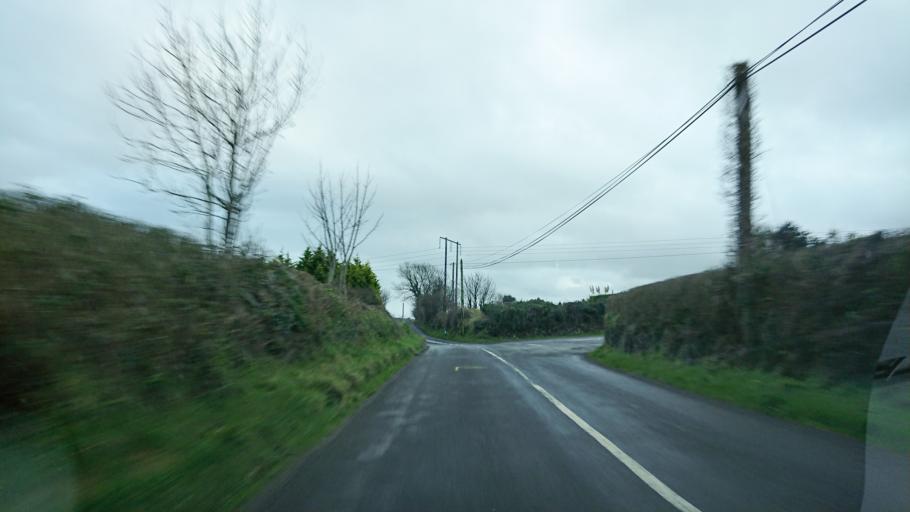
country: IE
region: Munster
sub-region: Waterford
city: Portlaw
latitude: 52.1708
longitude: -7.3958
